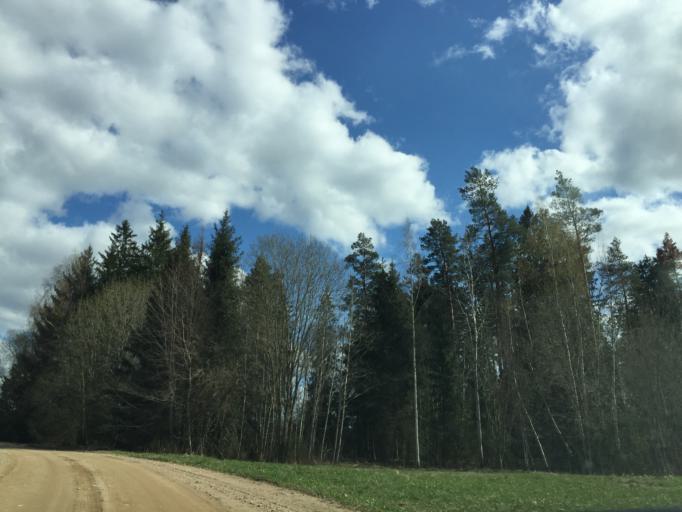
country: LV
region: Rezekne
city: Rezekne
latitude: 56.6566
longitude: 27.2736
